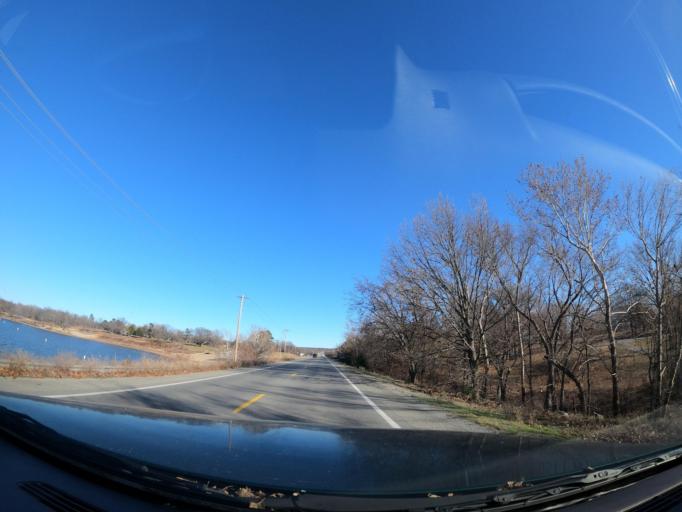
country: US
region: Oklahoma
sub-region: Pittsburg County
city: Longtown
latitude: 35.2392
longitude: -95.4958
